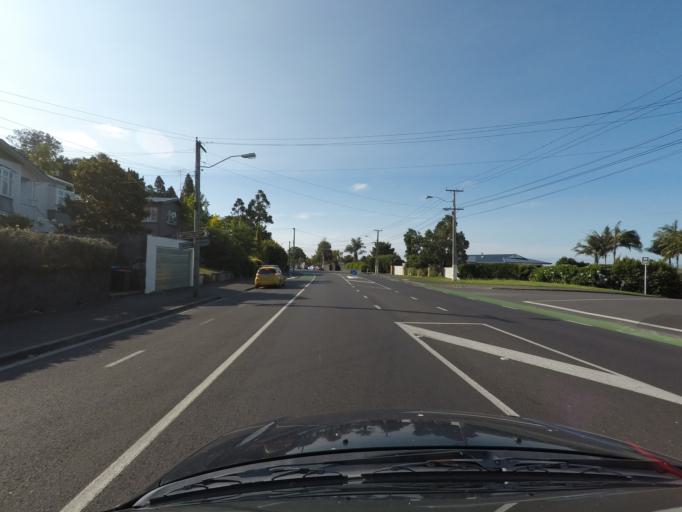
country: NZ
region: Auckland
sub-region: Auckland
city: Auckland
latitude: -36.8901
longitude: 174.7241
